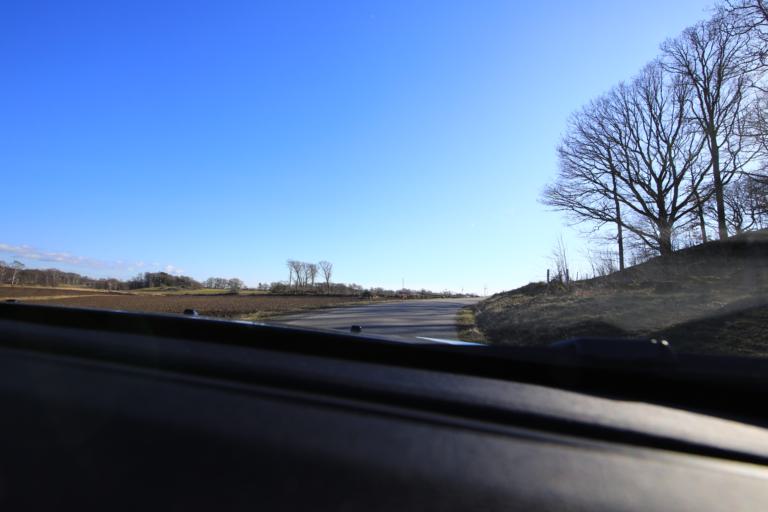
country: SE
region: Halland
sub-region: Varbergs Kommun
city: Tvaaker
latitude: 57.0604
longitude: 12.3744
